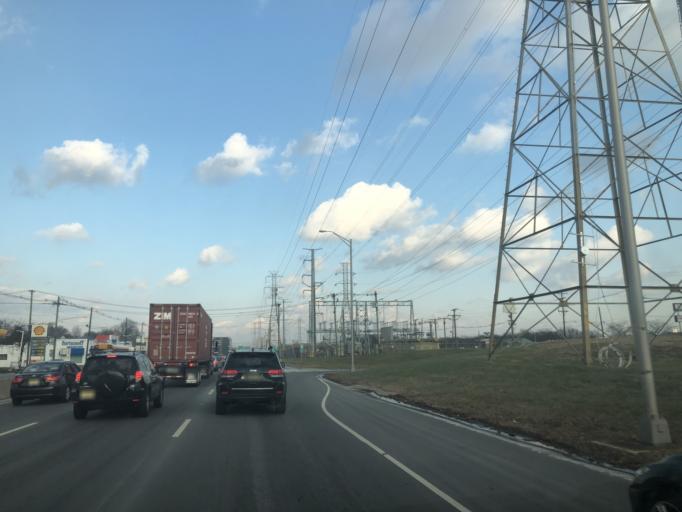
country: US
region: New Jersey
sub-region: Middlesex County
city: Fords
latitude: 40.5497
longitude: -74.3268
